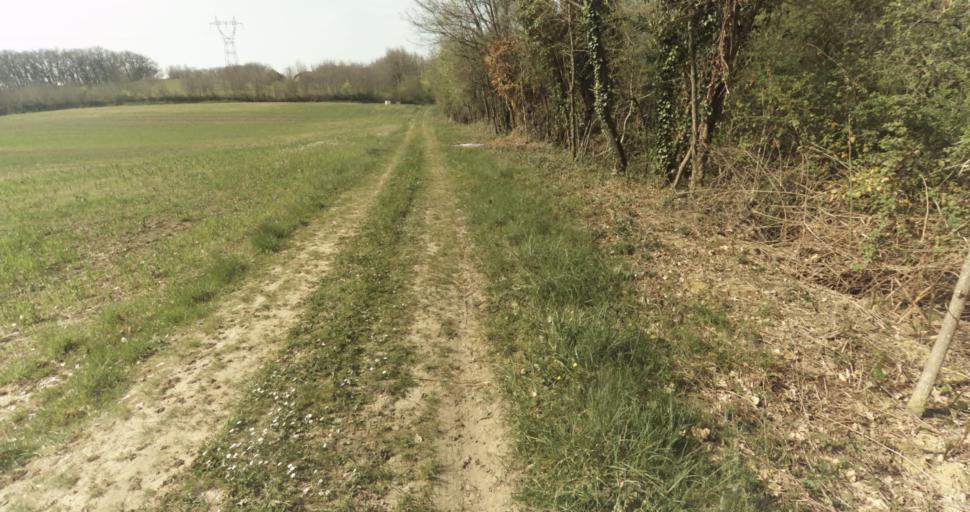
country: FR
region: Midi-Pyrenees
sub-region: Departement du Tarn-et-Garonne
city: Lafrancaise
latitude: 44.1344
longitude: 1.1723
